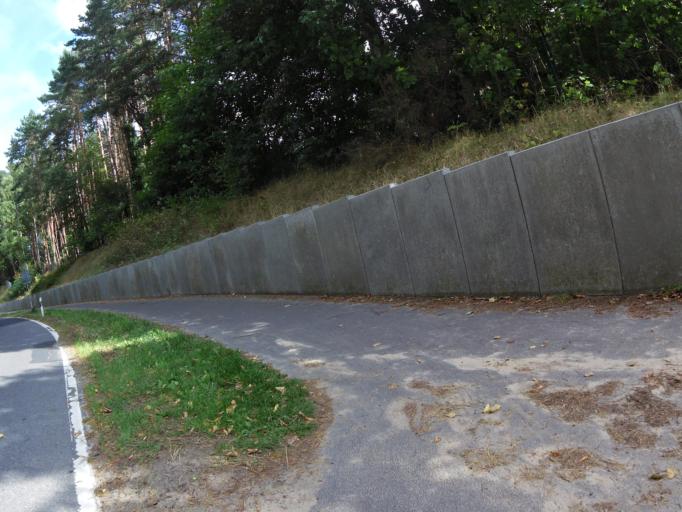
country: DE
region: Mecklenburg-Vorpommern
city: Seebad Bansin
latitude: 53.9406
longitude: 14.0772
